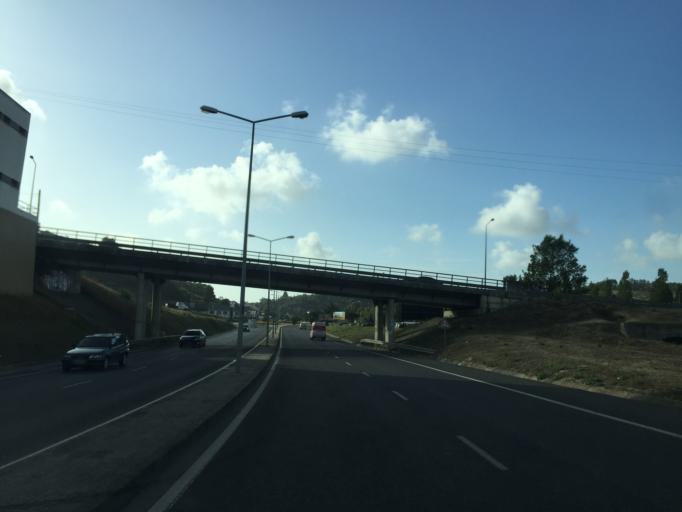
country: PT
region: Lisbon
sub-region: Torres Vedras
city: Torres Vedras
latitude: 39.0903
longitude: -9.2648
